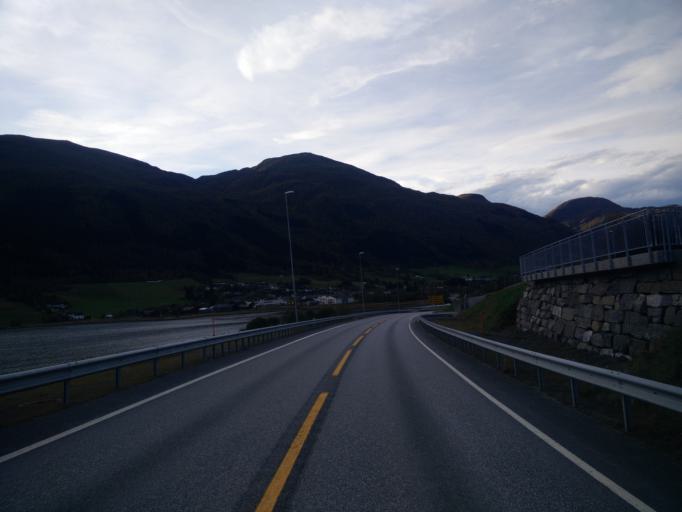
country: NO
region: More og Romsdal
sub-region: Gjemnes
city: Batnfjordsora
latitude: 62.9011
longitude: 7.6769
